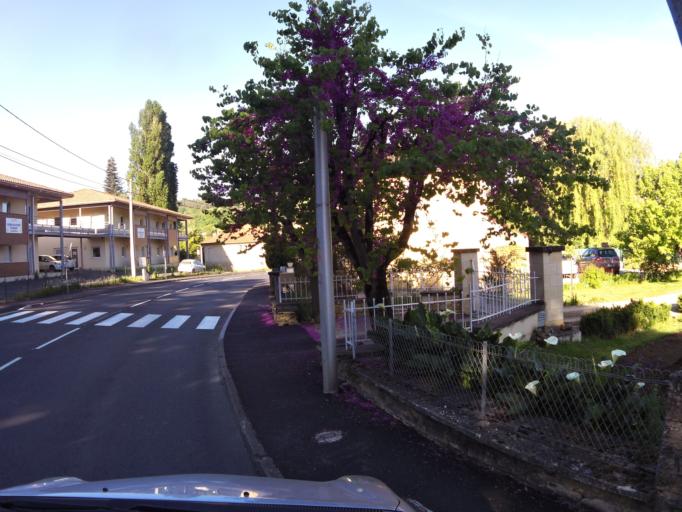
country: FR
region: Aquitaine
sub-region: Departement de la Dordogne
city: Sarlat-la-Caneda
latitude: 44.8979
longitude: 1.2172
